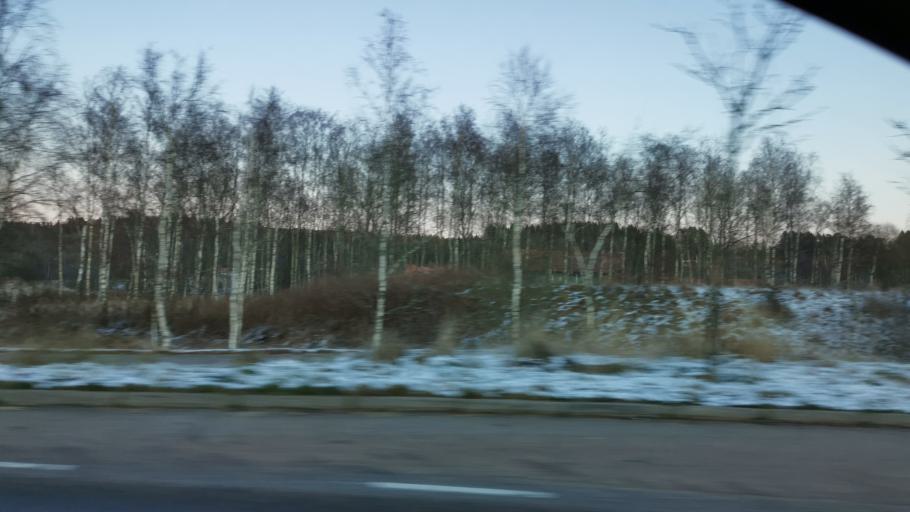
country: SE
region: Vaestra Goetaland
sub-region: Munkedals Kommun
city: Munkedal
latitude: 58.3992
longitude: 11.7492
